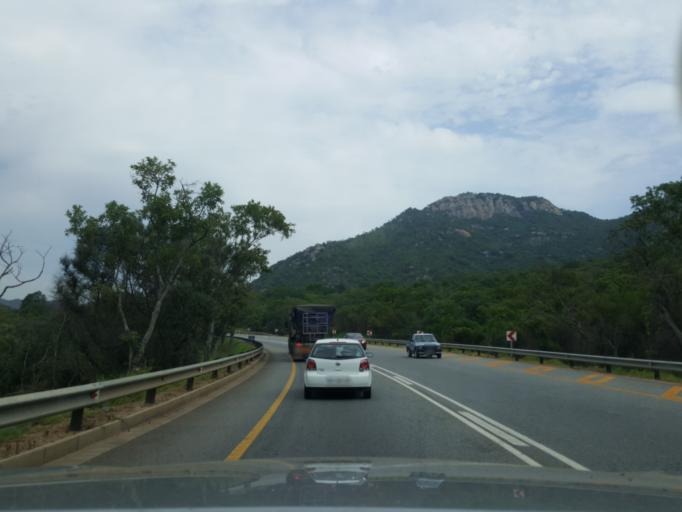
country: ZA
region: Mpumalanga
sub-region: Ehlanzeni District
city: Nelspruit
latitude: -25.5069
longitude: 31.1982
